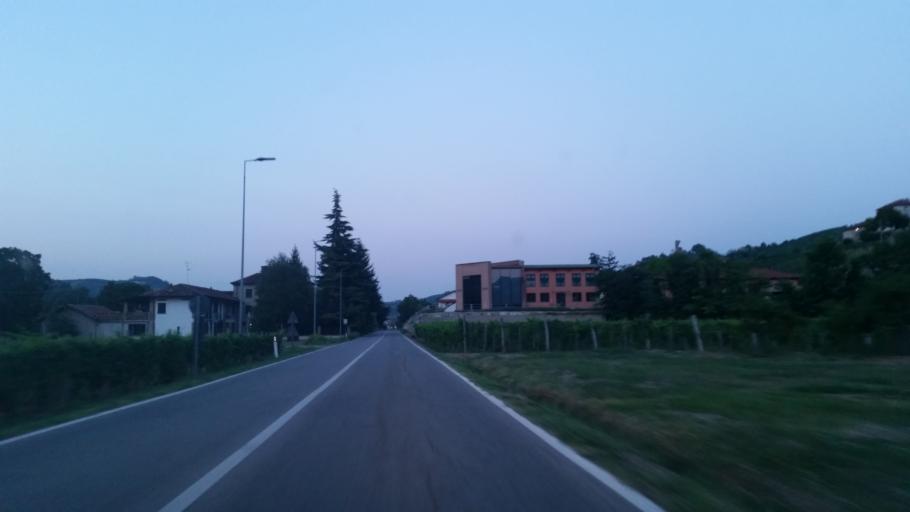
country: IT
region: Piedmont
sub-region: Provincia di Cuneo
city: Santo Stefano Belbo
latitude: 44.7013
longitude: 8.2197
